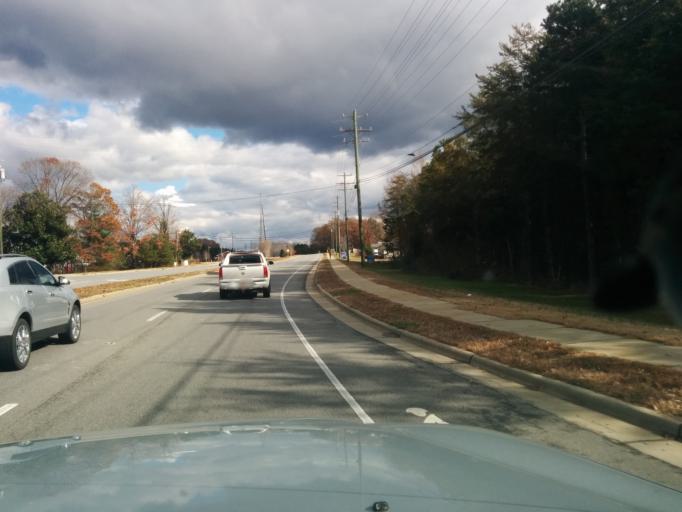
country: US
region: North Carolina
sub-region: Catawba County
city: Lake Norman of Catawba
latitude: 35.5729
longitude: -80.8948
